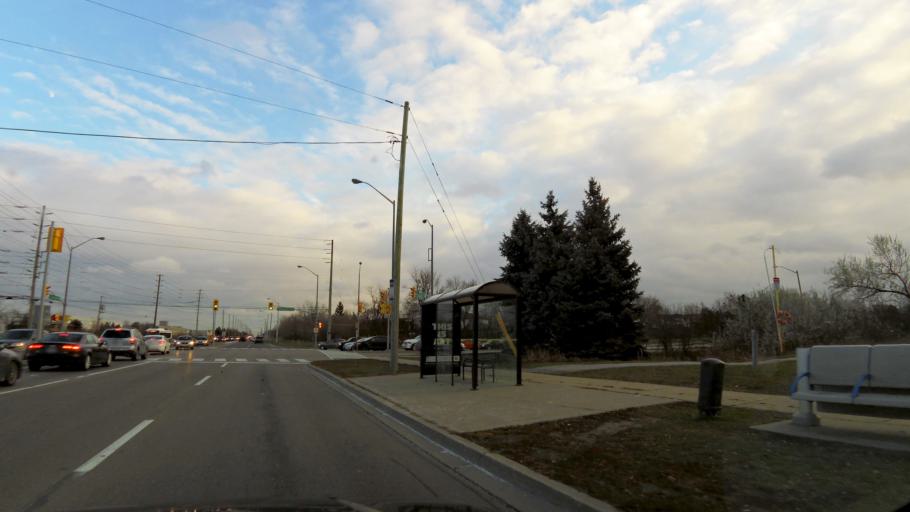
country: CA
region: Ontario
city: Brampton
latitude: 43.7445
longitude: -79.7208
